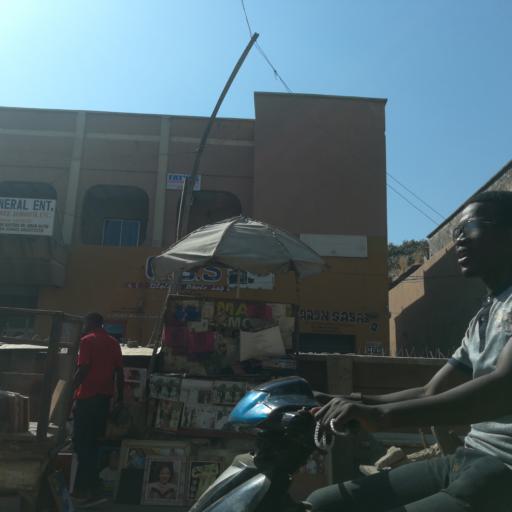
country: NG
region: Kano
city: Kano
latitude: 12.0105
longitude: 8.5336
